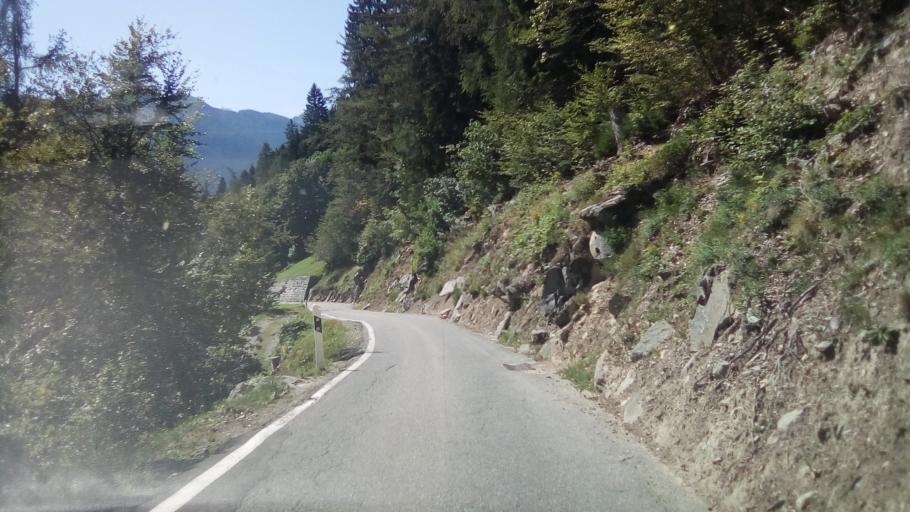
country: CH
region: Valais
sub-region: Saint-Maurice District
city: Salvan
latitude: 46.1300
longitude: 7.0189
